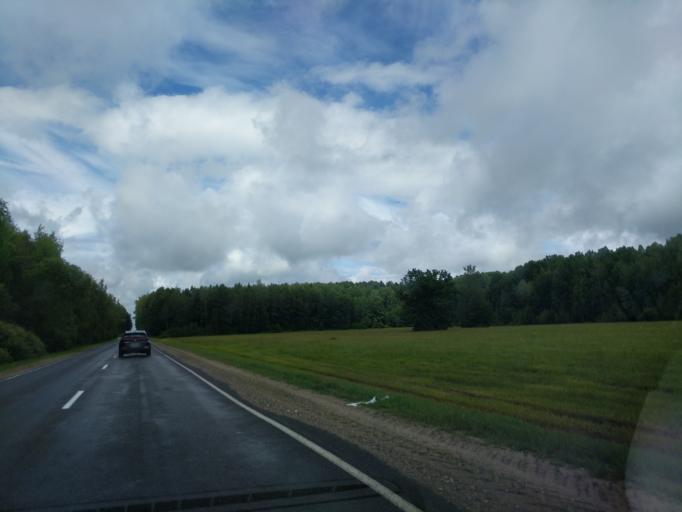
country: BY
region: Minsk
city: Il'ya
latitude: 54.3690
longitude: 27.3985
